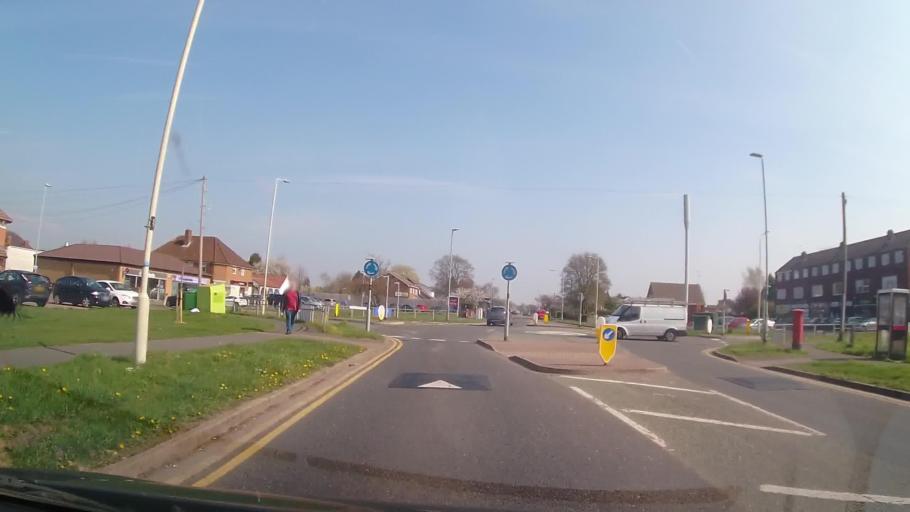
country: GB
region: England
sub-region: Leicestershire
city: Glenfield
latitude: 52.6455
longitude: -1.1947
